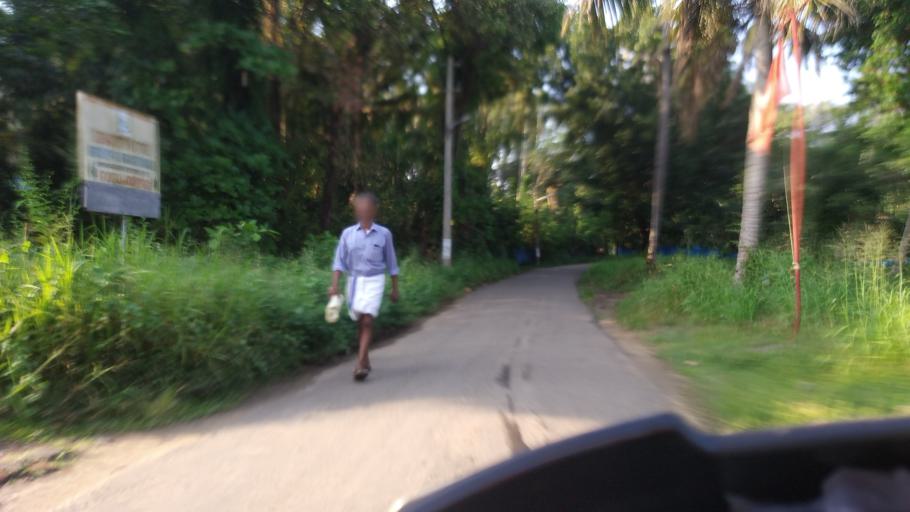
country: IN
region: Kerala
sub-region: Ernakulam
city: Elur
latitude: 10.0408
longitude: 76.2280
